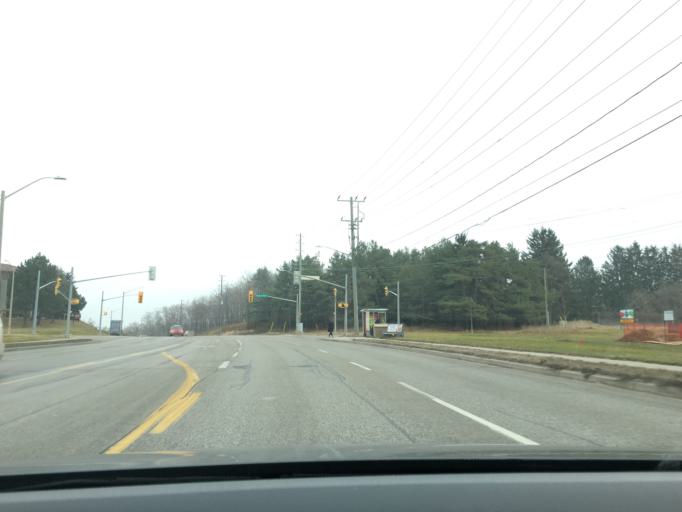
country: CA
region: Ontario
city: Barrie
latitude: 44.3508
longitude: -79.7005
